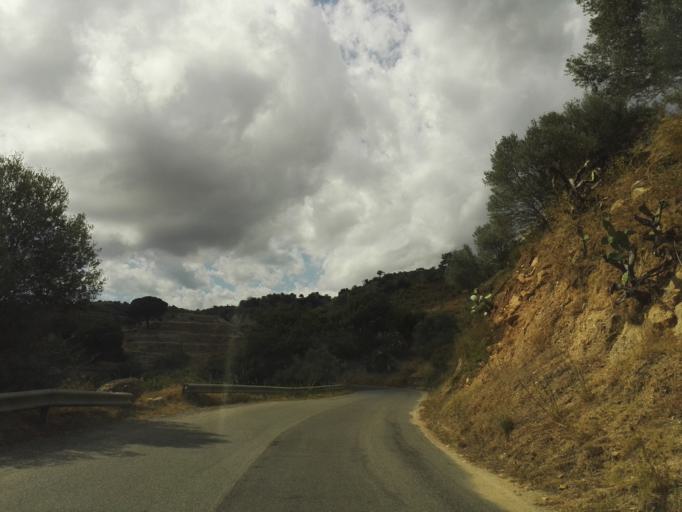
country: IT
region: Calabria
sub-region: Provincia di Reggio Calabria
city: Riace
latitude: 38.4243
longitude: 16.4855
